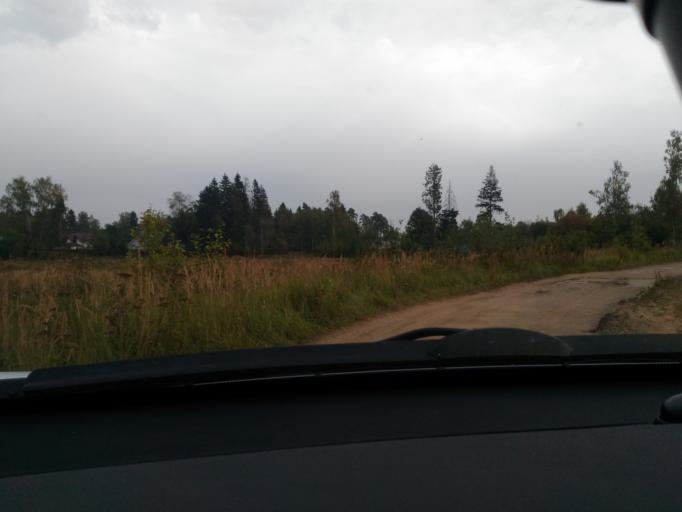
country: RU
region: Moskovskaya
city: Povarovo
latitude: 56.0926
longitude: 37.0611
